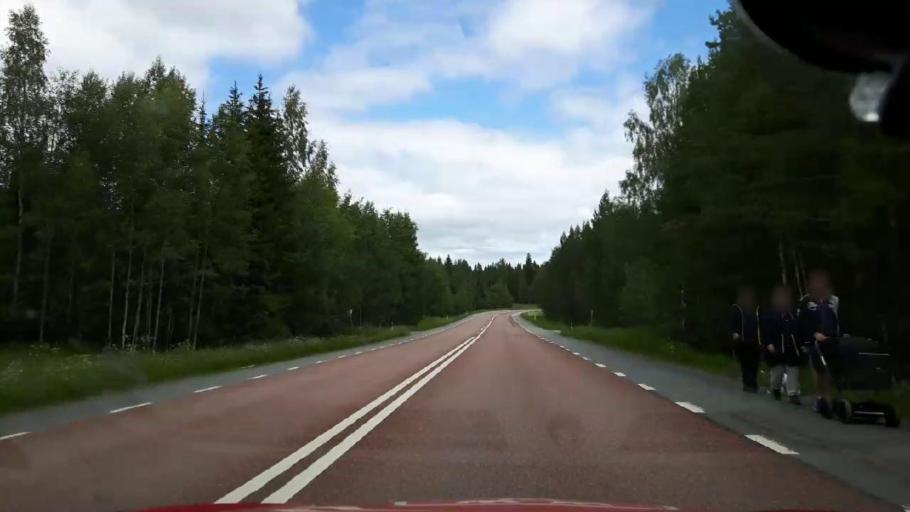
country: SE
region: Jaemtland
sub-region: OEstersunds Kommun
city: Brunflo
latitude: 62.9470
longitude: 15.0837
